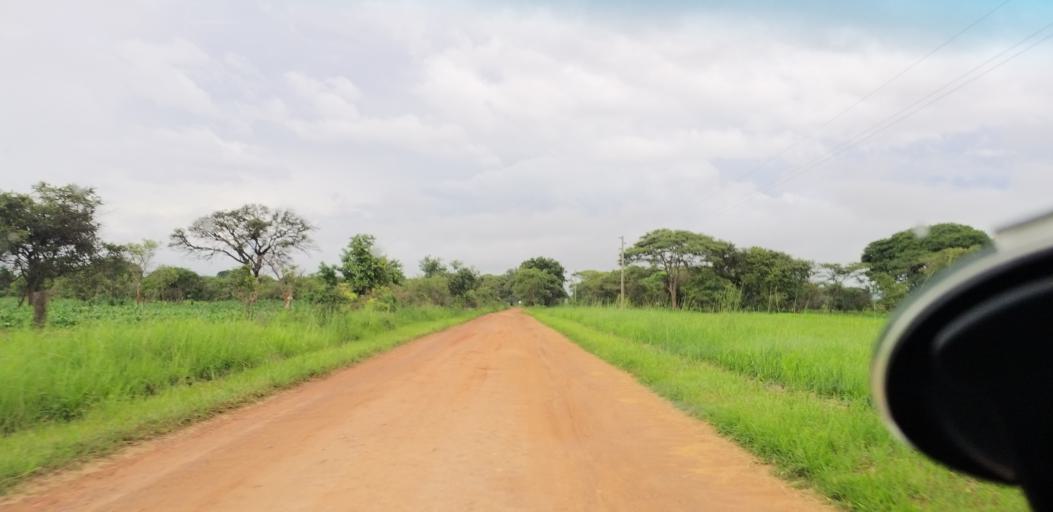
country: ZM
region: Lusaka
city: Lusaka
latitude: -15.5256
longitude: 28.3102
